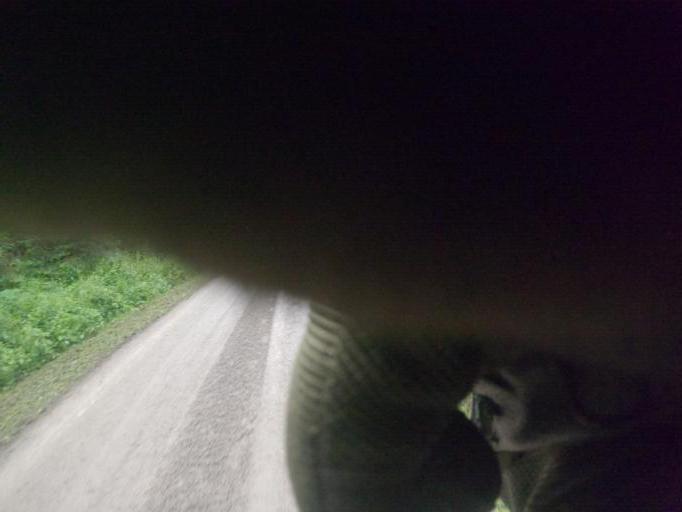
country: DE
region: Baden-Wuerttemberg
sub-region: Regierungsbezirk Stuttgart
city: Schorndorf
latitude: 48.7665
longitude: 9.5382
